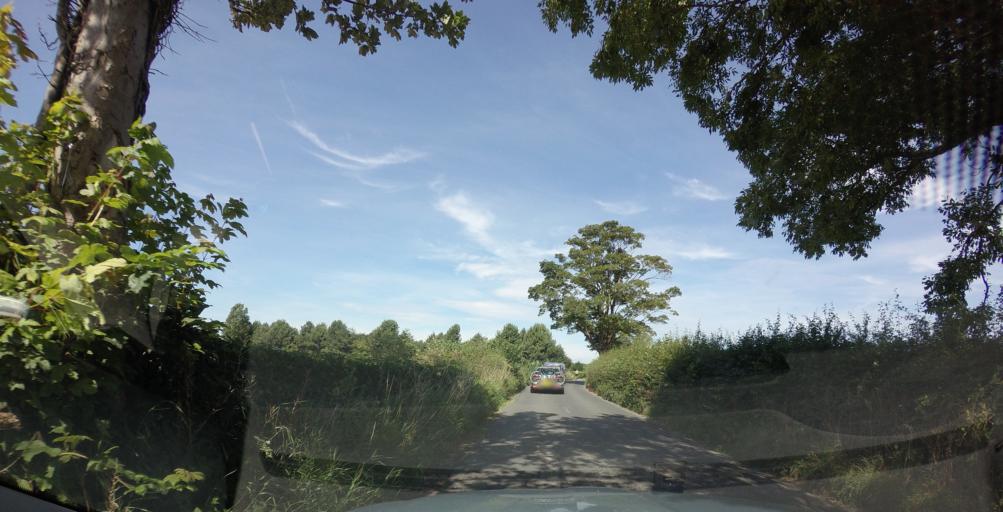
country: GB
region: England
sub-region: North Yorkshire
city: Ripon
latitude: 54.1258
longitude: -1.4870
